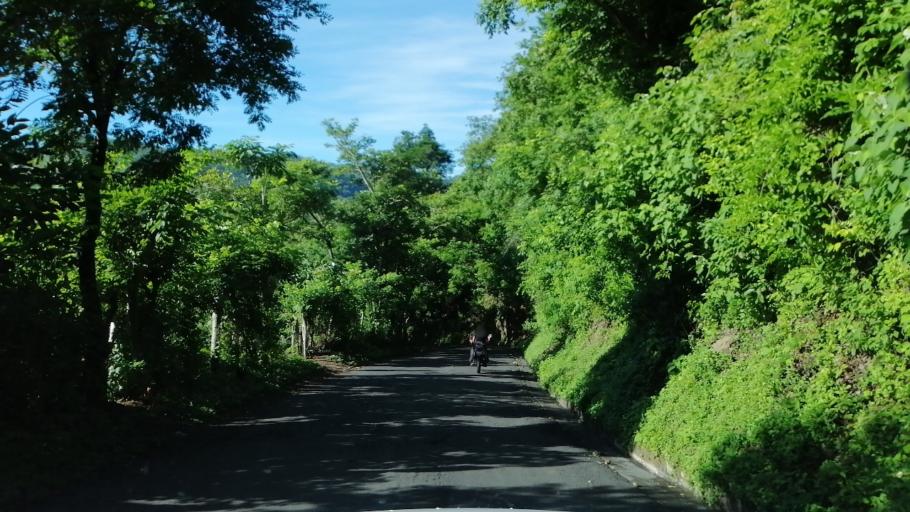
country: SV
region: Morazan
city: Cacaopera
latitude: 13.7718
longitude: -88.0745
